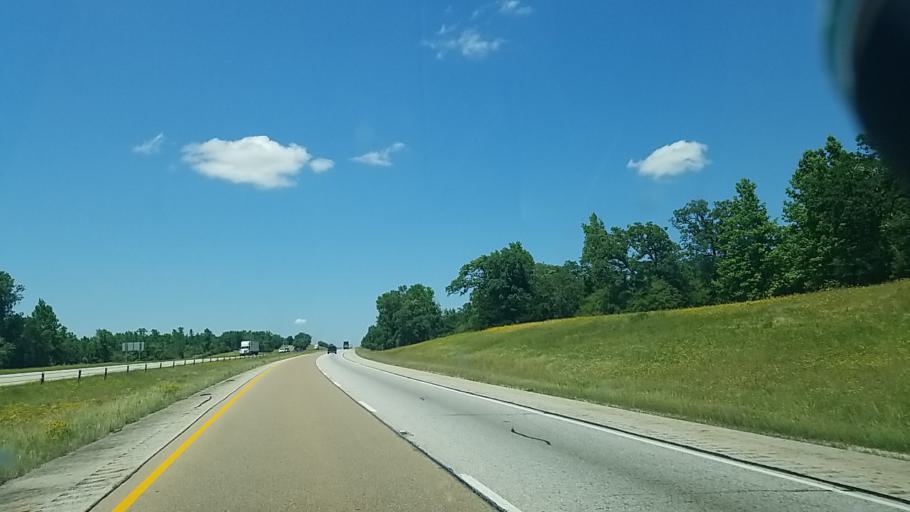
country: US
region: Texas
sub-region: Leon County
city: Centerville
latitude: 31.2121
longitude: -95.9968
